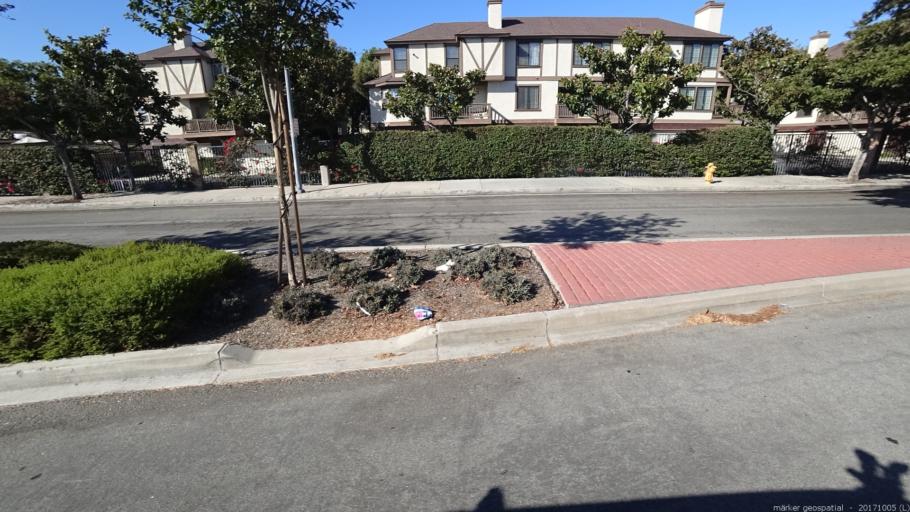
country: US
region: California
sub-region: Orange County
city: Garden Grove
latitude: 33.7760
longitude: -117.9388
